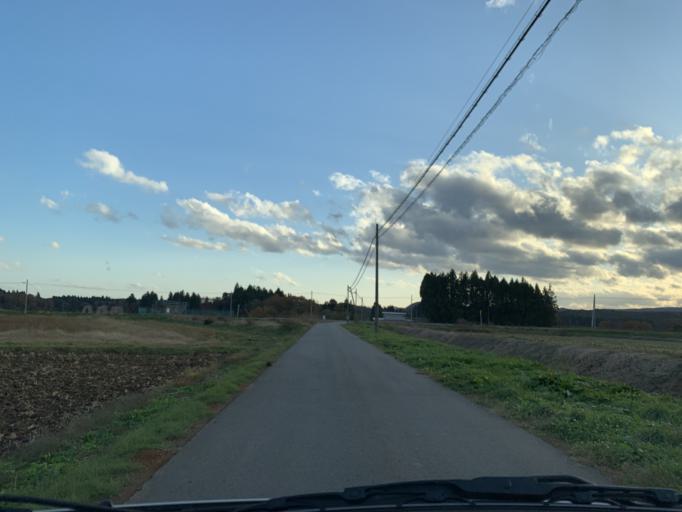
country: JP
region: Iwate
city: Mizusawa
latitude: 39.0891
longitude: 141.0368
